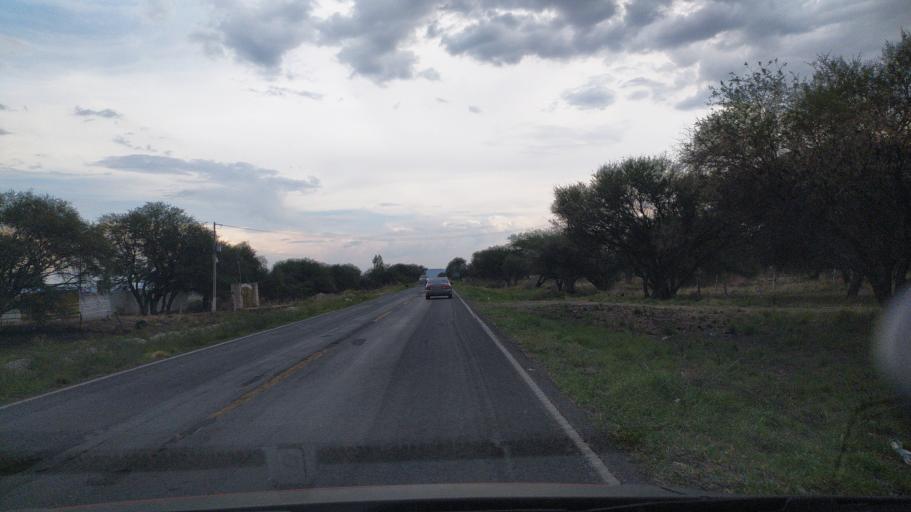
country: MX
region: Guanajuato
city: Ciudad Manuel Doblado
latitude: 20.7672
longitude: -101.9142
